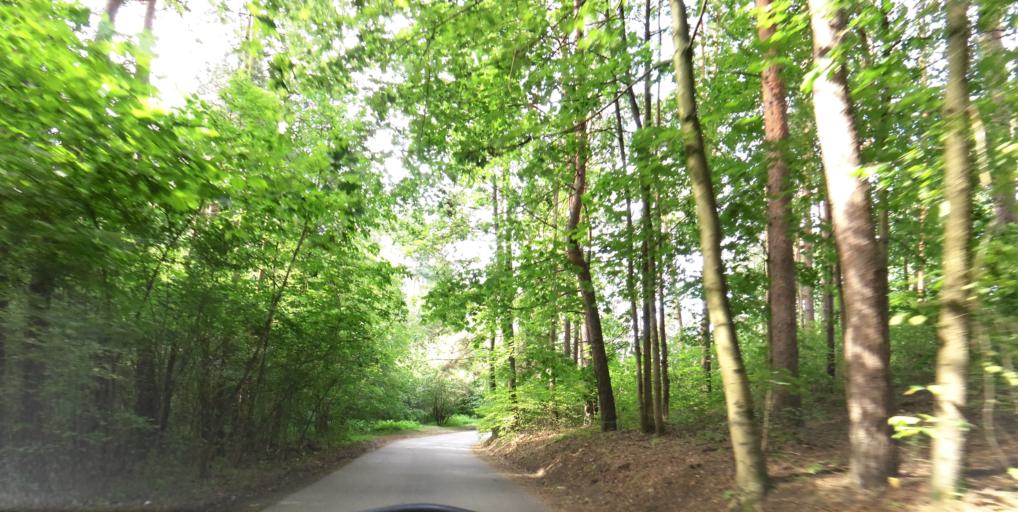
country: LT
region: Vilnius County
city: Seskine
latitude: 54.7301
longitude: 25.2857
